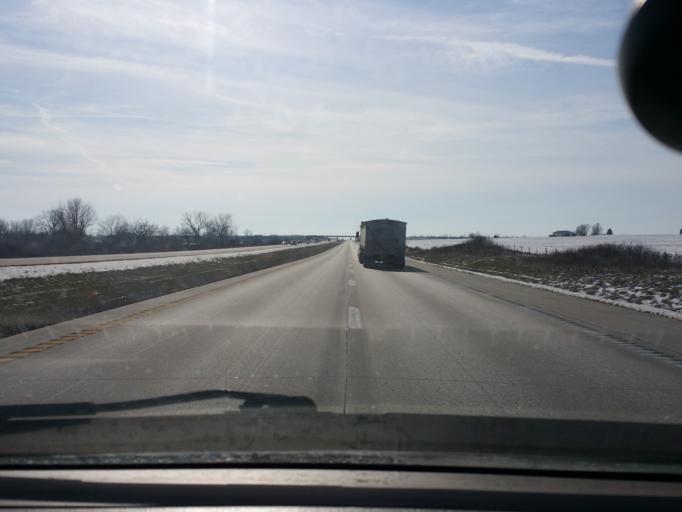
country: US
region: Missouri
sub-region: Clinton County
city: Cameron
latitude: 39.6403
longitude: -94.2427
